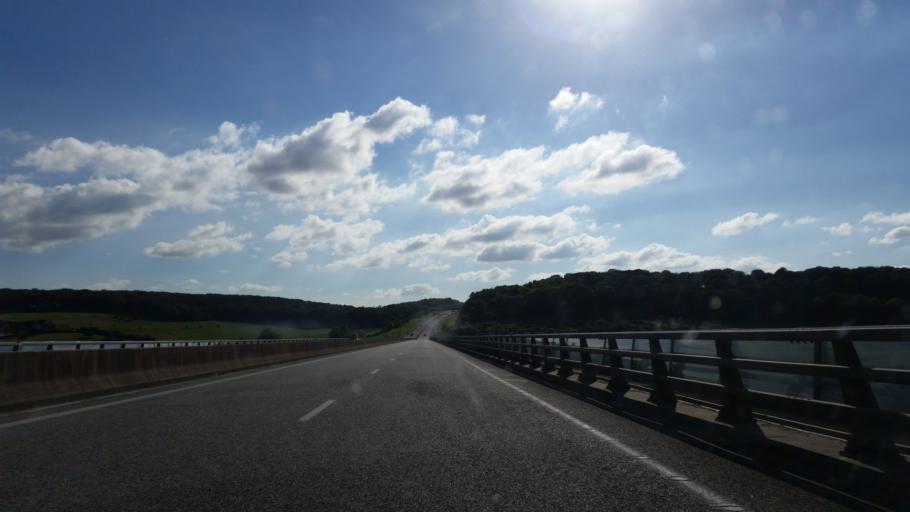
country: FR
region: Haute-Normandie
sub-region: Departement de la Seine-Maritime
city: Aumale
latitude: 49.7836
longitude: 1.7573
